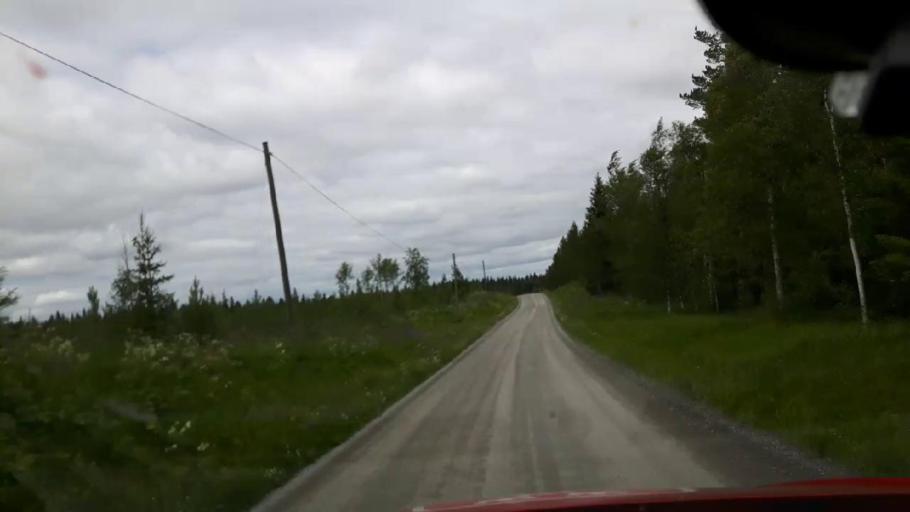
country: SE
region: Jaemtland
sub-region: OEstersunds Kommun
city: Brunflo
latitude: 63.0573
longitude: 14.9117
